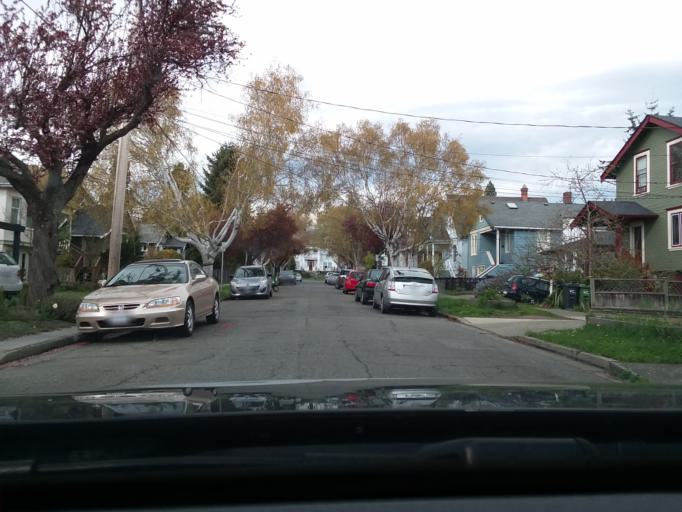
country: CA
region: British Columbia
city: Victoria
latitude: 48.4179
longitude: -123.3492
